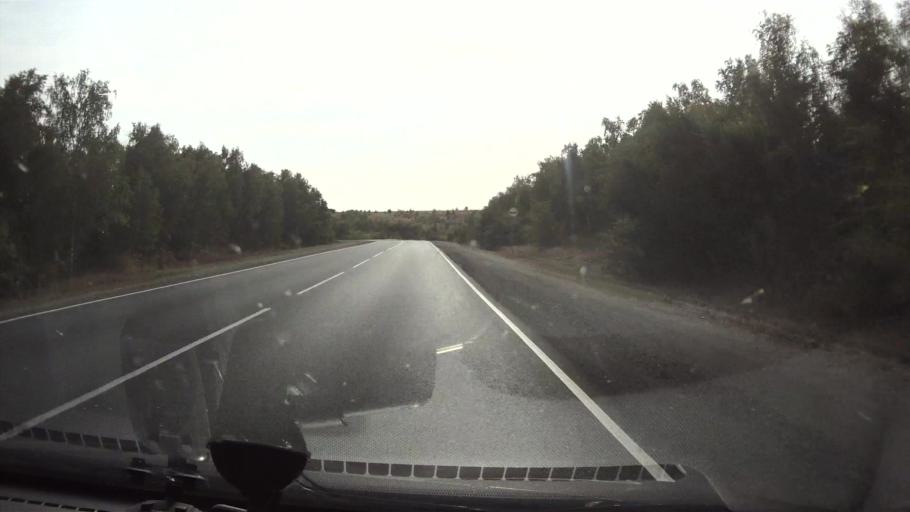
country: RU
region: Saratov
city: Sennoy
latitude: 52.1036
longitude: 46.8184
